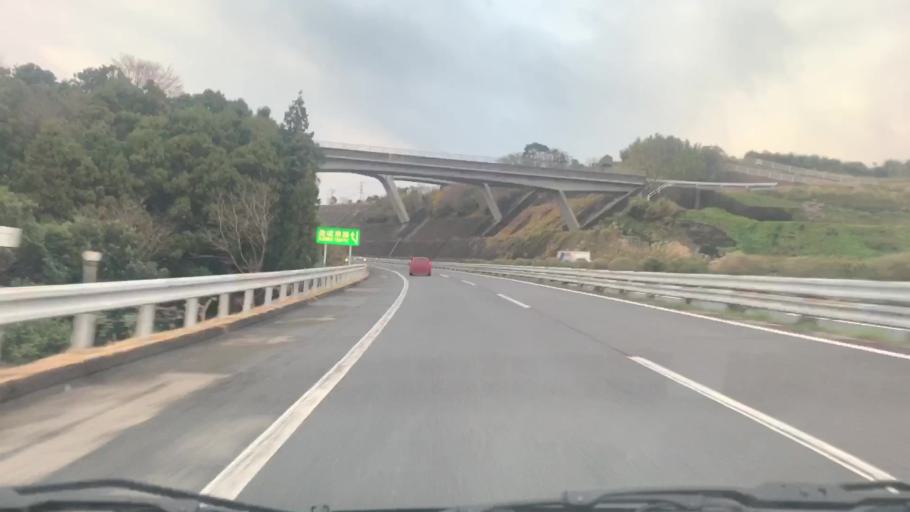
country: JP
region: Nagasaki
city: Omura
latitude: 33.0005
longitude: 129.9513
